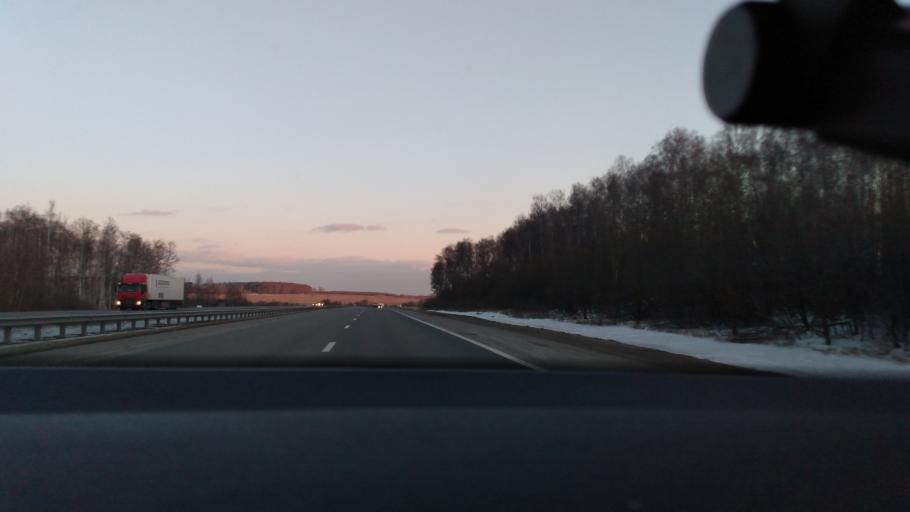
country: RU
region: Moskovskaya
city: Kolomna
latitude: 55.1080
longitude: 38.8824
